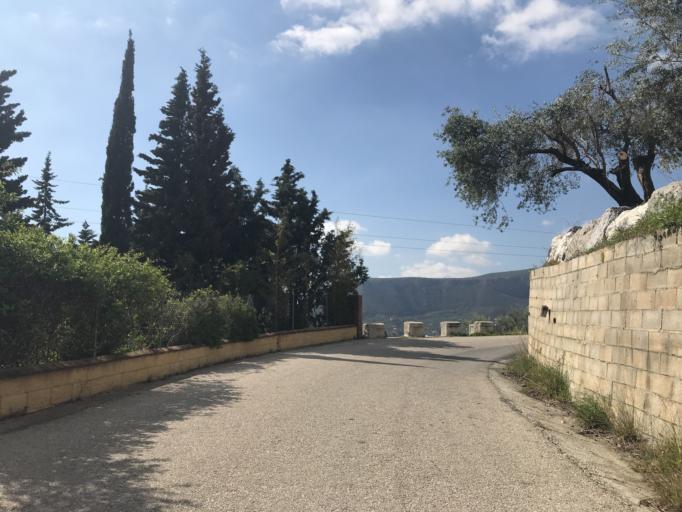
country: ES
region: Andalusia
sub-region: Provincia de Malaga
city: Alcaucin
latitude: 36.9081
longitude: -4.1110
